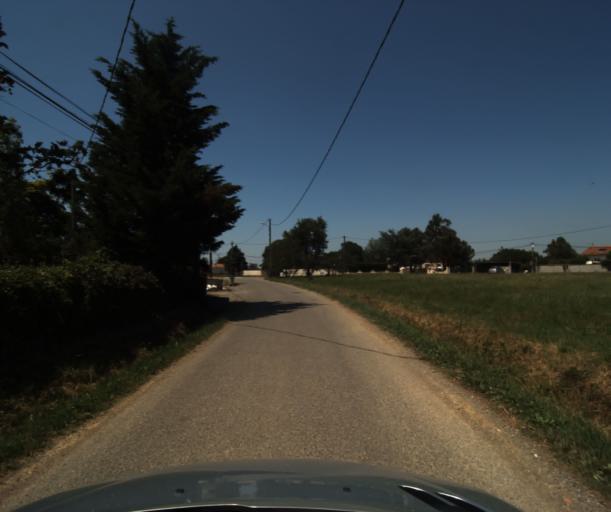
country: FR
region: Midi-Pyrenees
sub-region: Departement de la Haute-Garonne
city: Saubens
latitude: 43.4752
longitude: 1.3589
